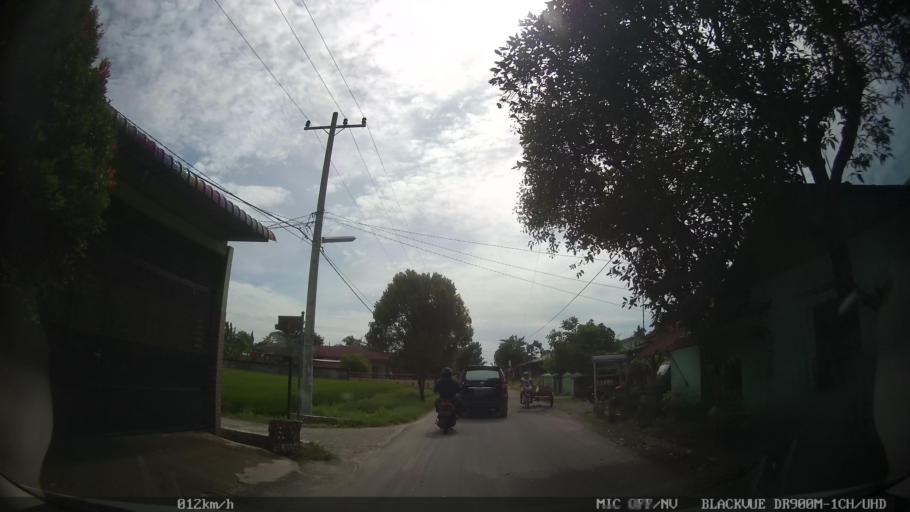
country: ID
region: North Sumatra
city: Percut
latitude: 3.6199
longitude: 98.7976
